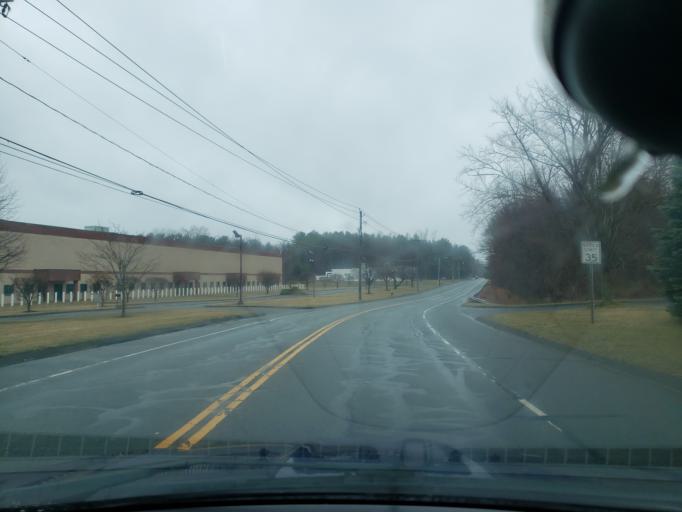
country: US
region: Connecticut
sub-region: Hartford County
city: Windsor
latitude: 41.8697
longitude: -72.6876
